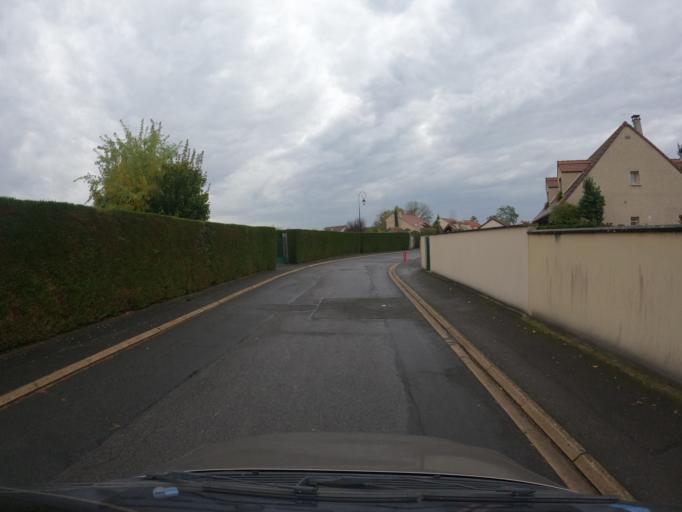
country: FR
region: Ile-de-France
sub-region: Departement de Seine-et-Marne
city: Villeneuve-le-Comte
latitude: 48.8164
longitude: 2.8284
